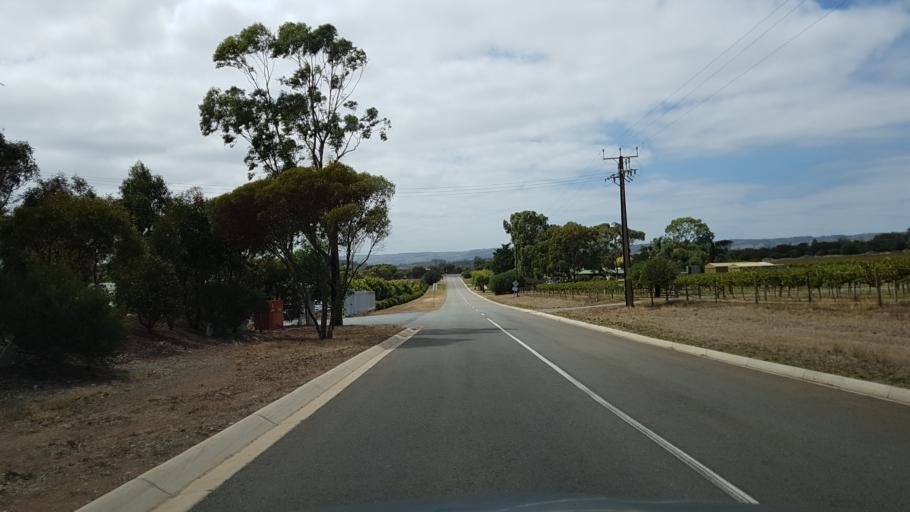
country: AU
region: South Australia
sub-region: Onkaparinga
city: McLaren Vale
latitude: -35.2105
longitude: 138.5175
